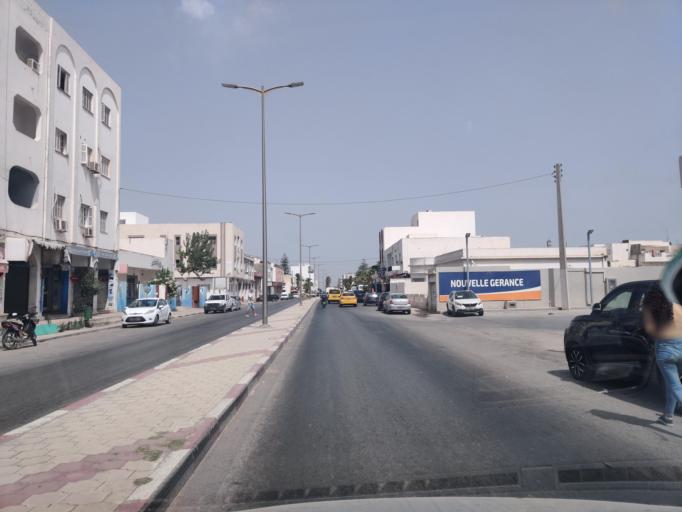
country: TN
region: Nabul
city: Bu `Urqub
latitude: 36.5952
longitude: 10.5013
